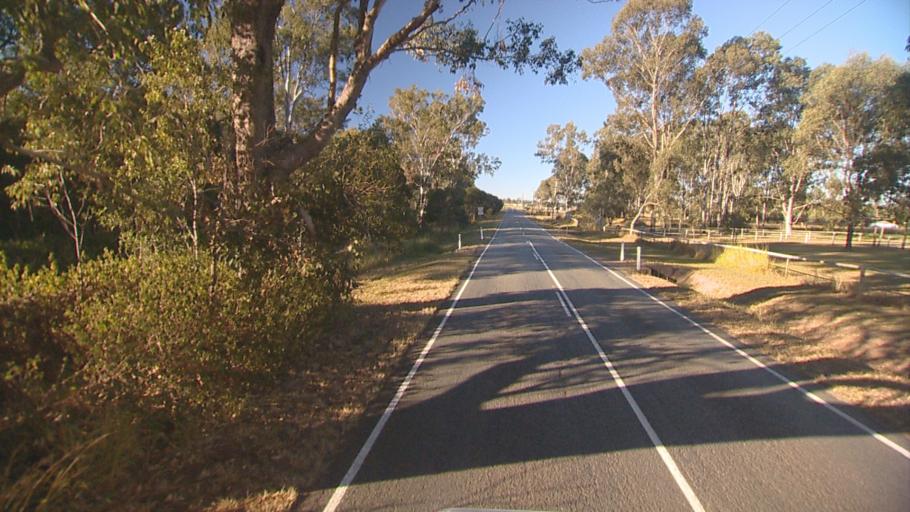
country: AU
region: Queensland
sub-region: Logan
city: Chambers Flat
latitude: -27.7547
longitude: 153.0882
